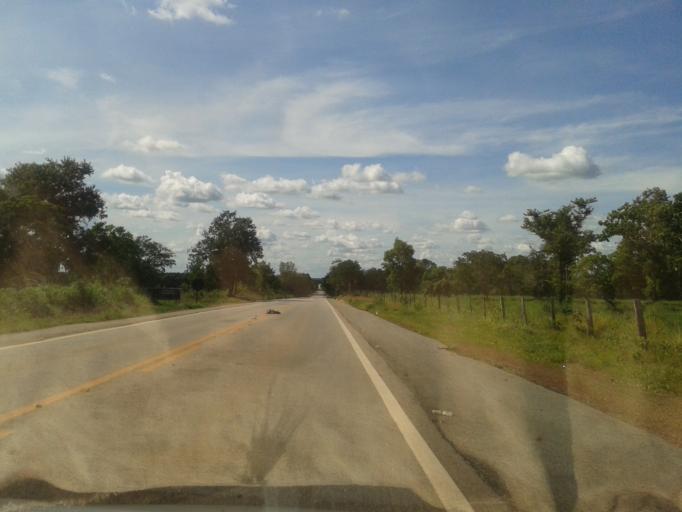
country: BR
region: Goias
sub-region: Mozarlandia
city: Mozarlandia
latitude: -15.2430
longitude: -50.5095
